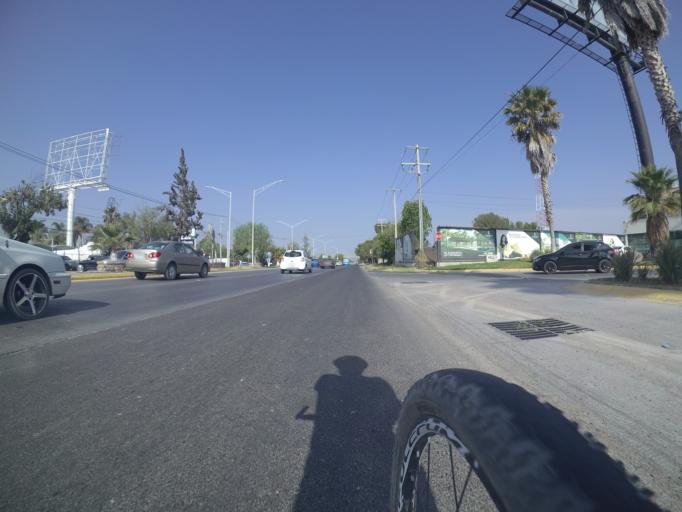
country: MX
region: Aguascalientes
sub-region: Jesus Maria
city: El Llano
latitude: 21.9489
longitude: -102.3134
